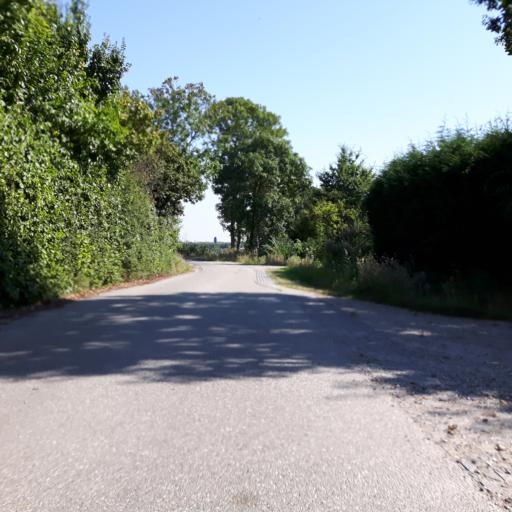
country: NL
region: Zeeland
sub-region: Gemeente Vlissingen
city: Vlissingen
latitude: 51.4475
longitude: 3.6143
